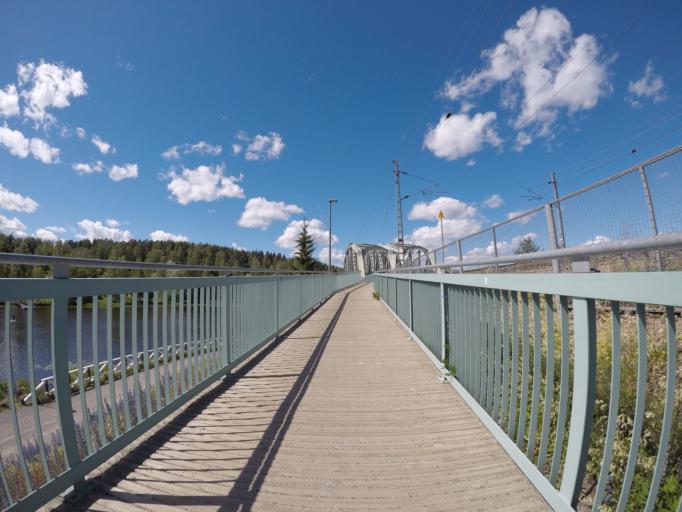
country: FI
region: Haeme
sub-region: Haemeenlinna
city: Haemeenlinna
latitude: 61.0146
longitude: 24.4485
